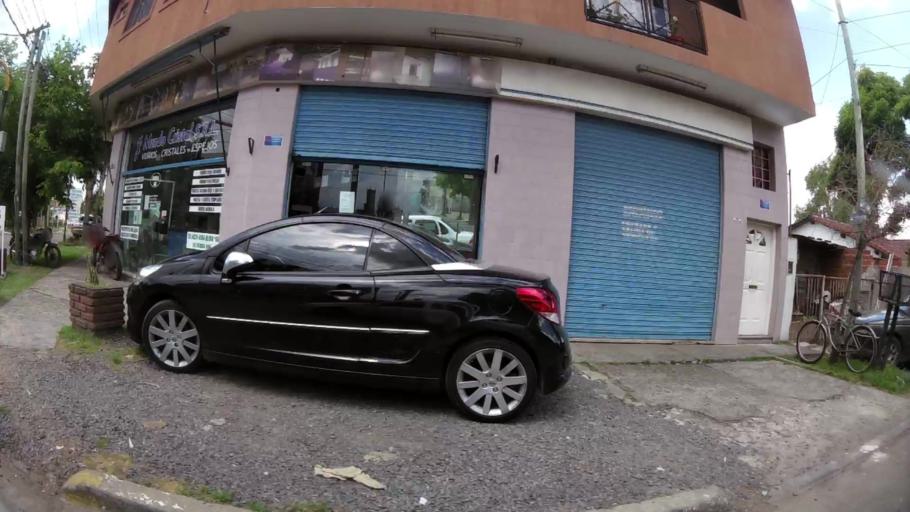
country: AR
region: Buenos Aires
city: Ituzaingo
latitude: -34.6386
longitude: -58.6715
